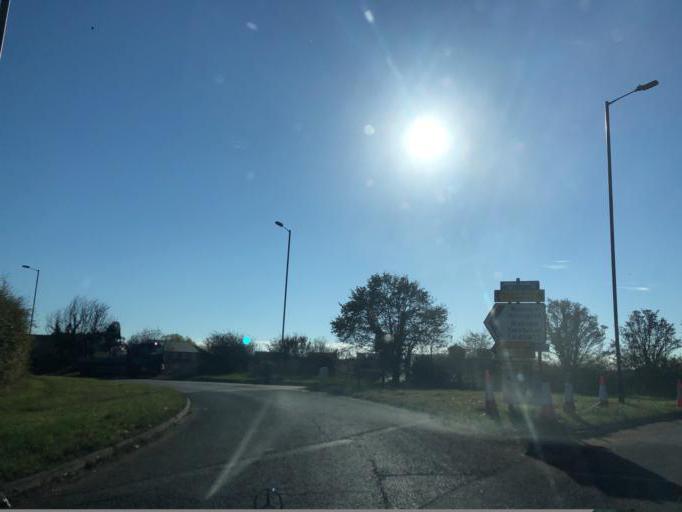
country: GB
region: England
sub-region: Warwickshire
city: Warwick
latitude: 52.2697
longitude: -1.5579
